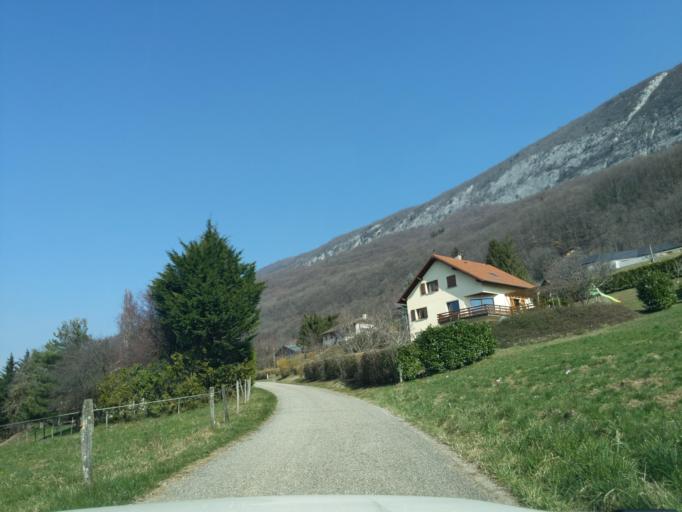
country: FR
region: Rhone-Alpes
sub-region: Departement de la Haute-Savoie
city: Moye
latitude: 45.8952
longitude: 5.8501
